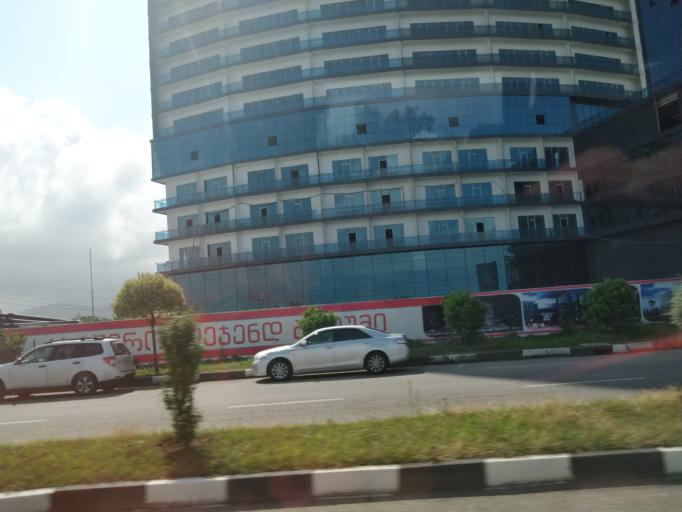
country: GE
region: Ajaria
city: Batumi
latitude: 41.6264
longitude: 41.5989
